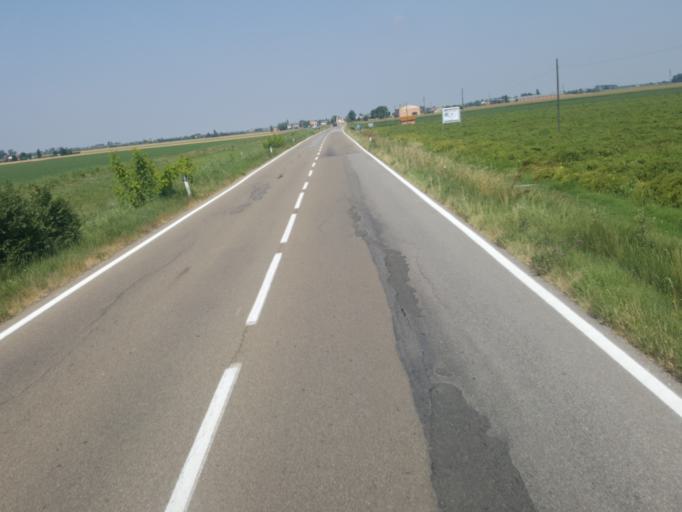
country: IT
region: Emilia-Romagna
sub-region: Provincia di Ravenna
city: Massa Lombarda
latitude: 44.4614
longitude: 11.7873
